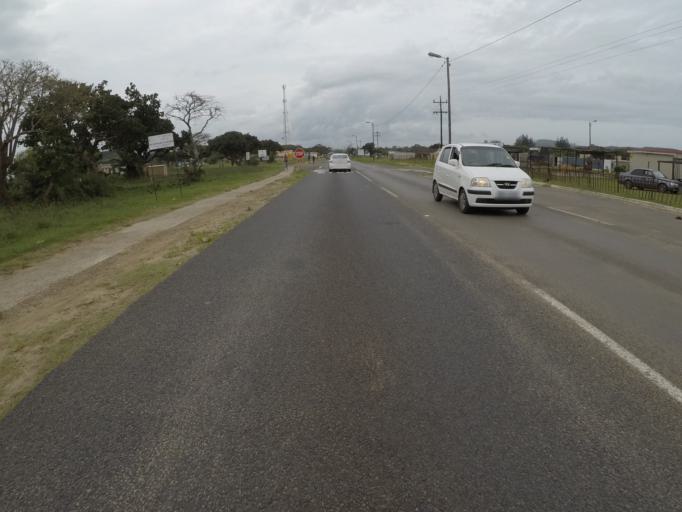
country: ZA
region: KwaZulu-Natal
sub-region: uThungulu District Municipality
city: Richards Bay
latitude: -28.7640
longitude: 32.1316
